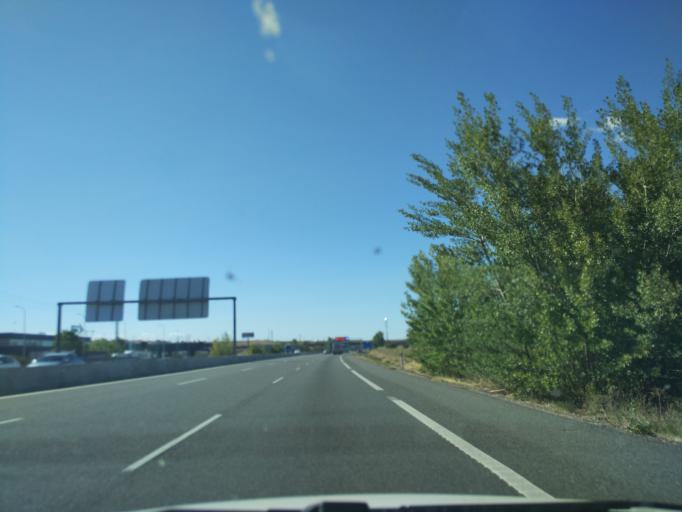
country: ES
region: Castille and Leon
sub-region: Provincia de Zamora
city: Benavente
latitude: 42.0033
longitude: -5.6592
